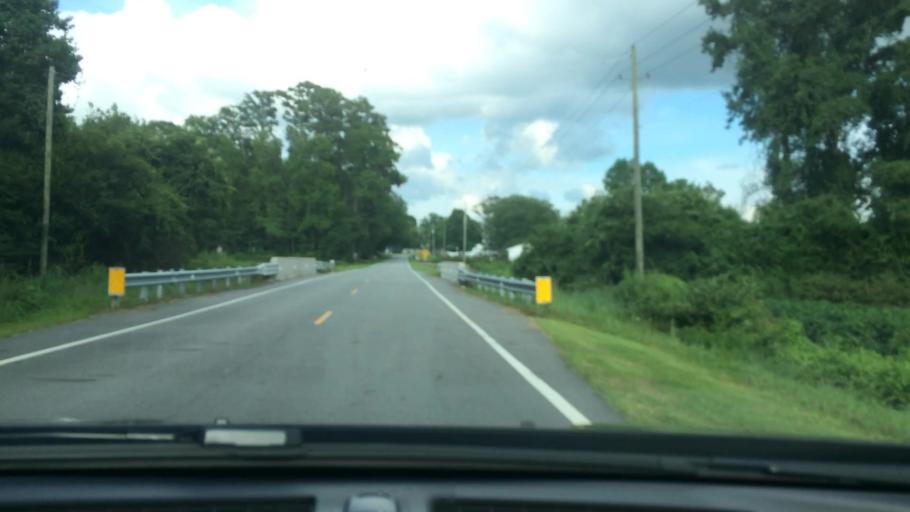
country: US
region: North Carolina
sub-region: Pitt County
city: Ayden
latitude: 35.4330
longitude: -77.4258
